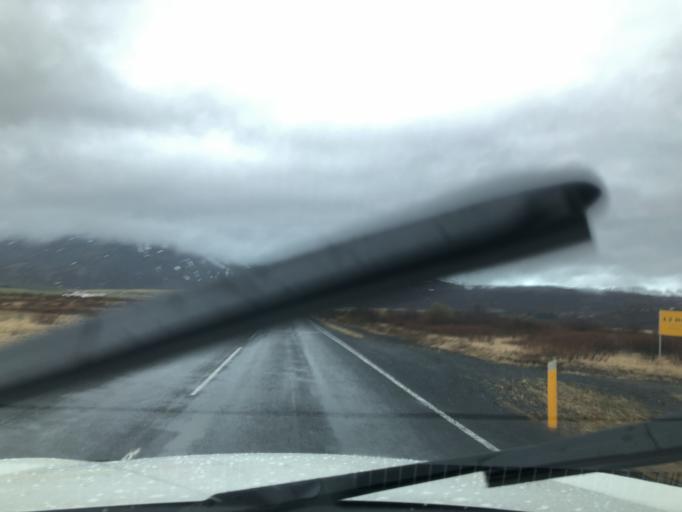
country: IS
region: South
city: Selfoss
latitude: 64.2373
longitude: -20.6489
